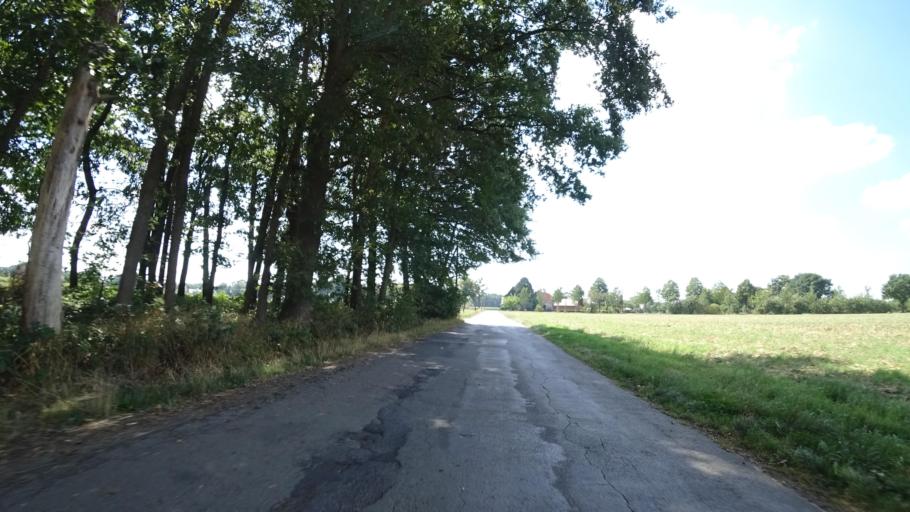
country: DE
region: North Rhine-Westphalia
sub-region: Regierungsbezirk Detmold
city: Rheda-Wiedenbruck
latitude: 51.8714
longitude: 8.2756
